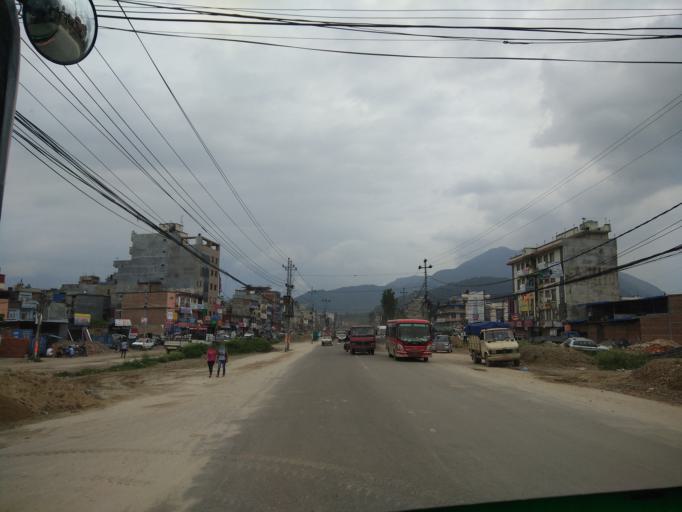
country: NP
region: Central Region
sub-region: Bagmati Zone
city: Kathmandu
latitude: 27.7353
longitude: 85.3195
